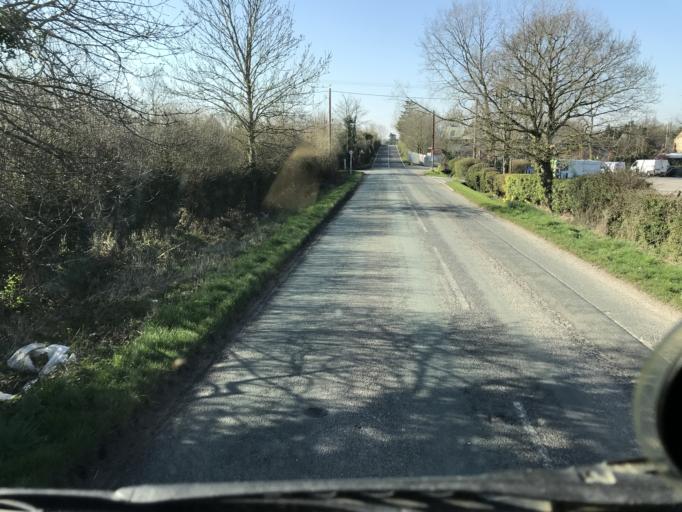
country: GB
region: England
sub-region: Cheshire West and Chester
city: Waverton
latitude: 53.1673
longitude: -2.8228
